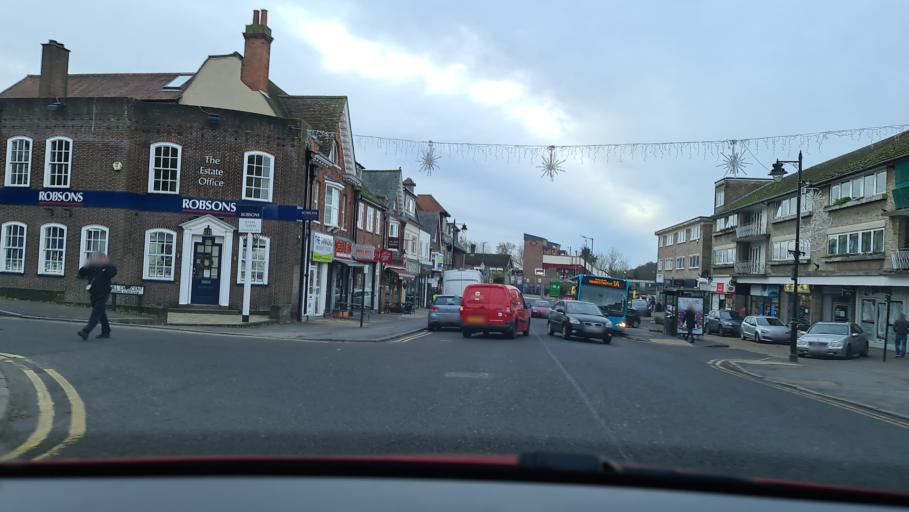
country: GB
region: England
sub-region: Buckinghamshire
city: Amersham on the Hill
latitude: 51.6754
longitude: -0.6076
